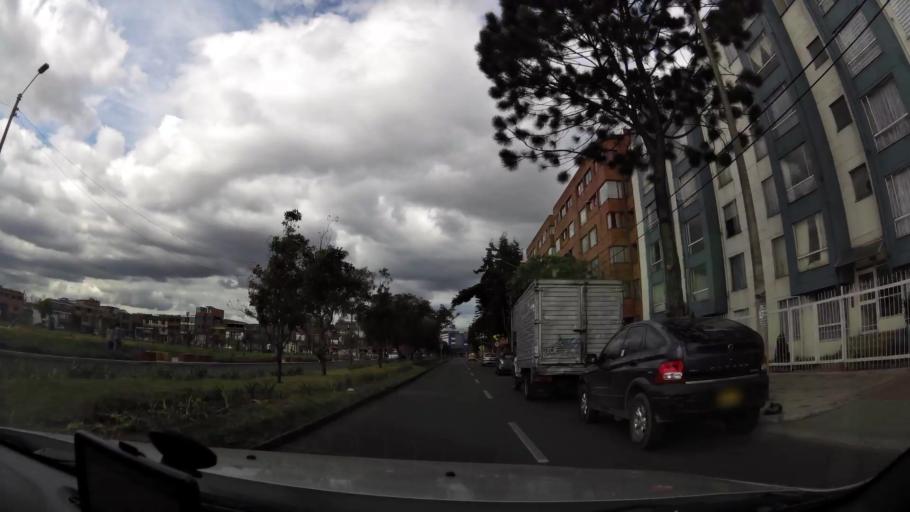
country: CO
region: Bogota D.C.
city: Bogota
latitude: 4.6101
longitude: -74.1350
